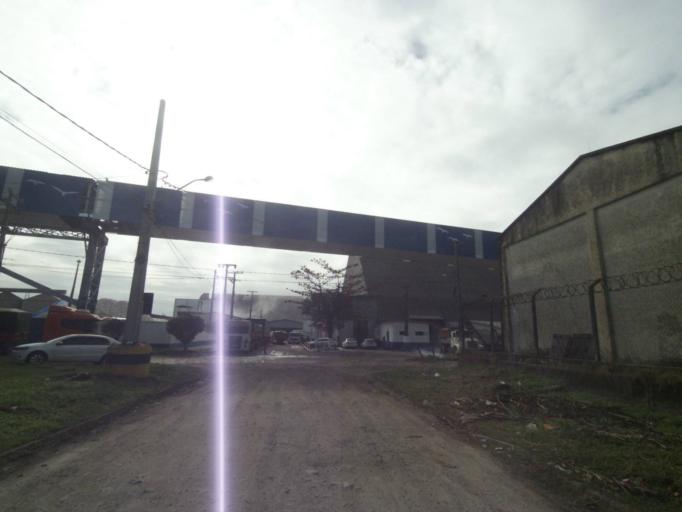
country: BR
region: Parana
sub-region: Paranagua
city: Paranagua
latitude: -25.5078
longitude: -48.5262
